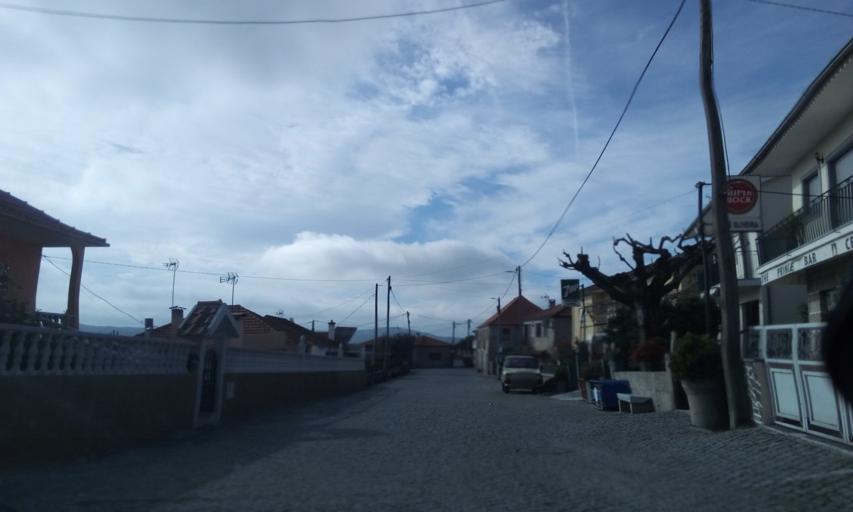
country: PT
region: Guarda
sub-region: Aguiar da Beira
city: Aguiar da Beira
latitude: 40.7309
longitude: -7.5564
